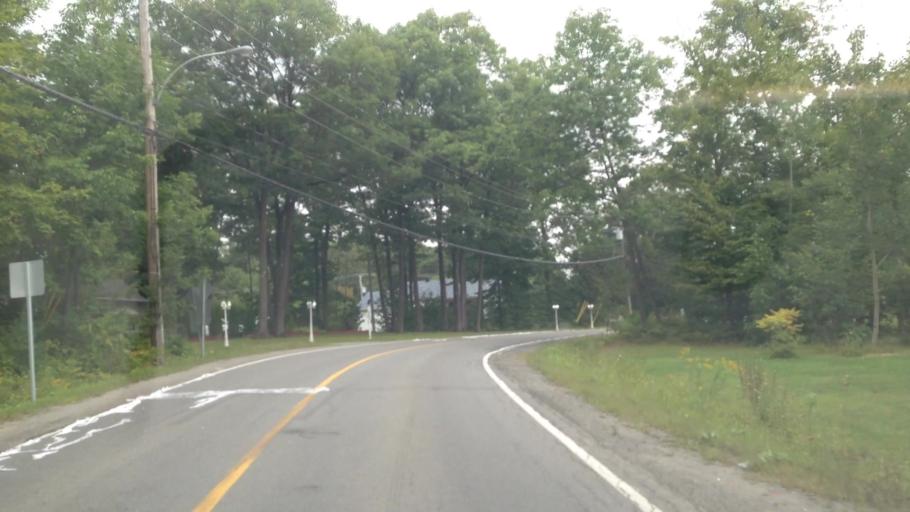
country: CA
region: Quebec
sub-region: Laurentides
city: Saint-Jerome
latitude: 45.8205
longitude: -73.9743
